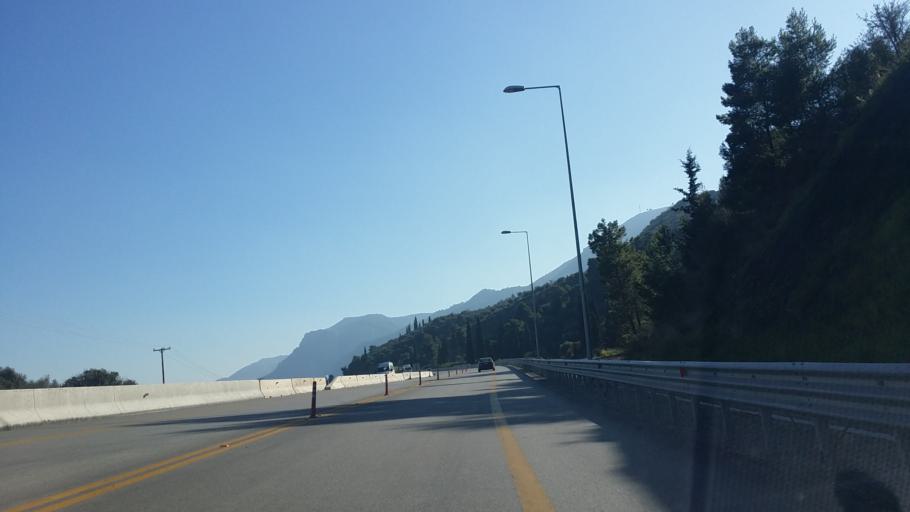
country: GR
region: West Greece
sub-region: Nomos Achaias
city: Temeni
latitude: 38.2073
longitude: 22.1368
